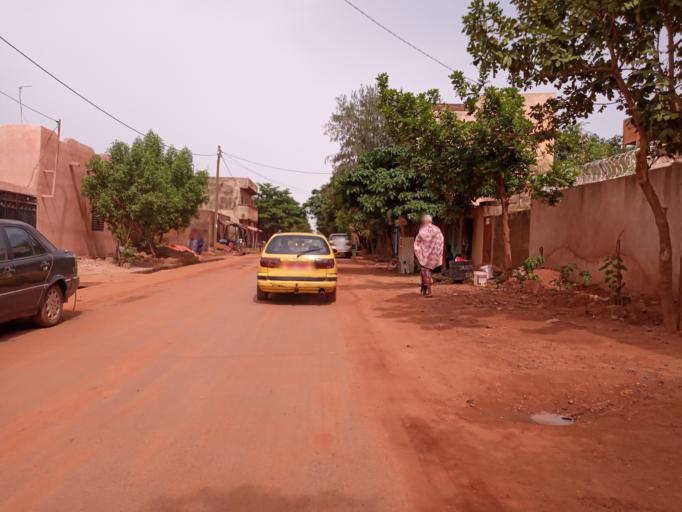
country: ML
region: Bamako
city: Bamako
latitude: 12.5535
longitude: -7.9958
